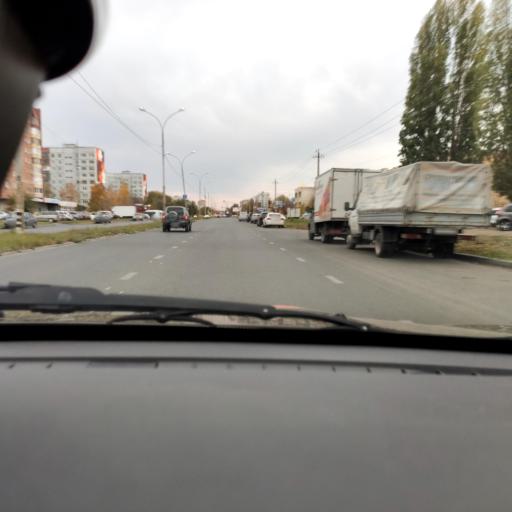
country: RU
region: Samara
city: Tol'yatti
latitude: 53.5389
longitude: 49.3149
